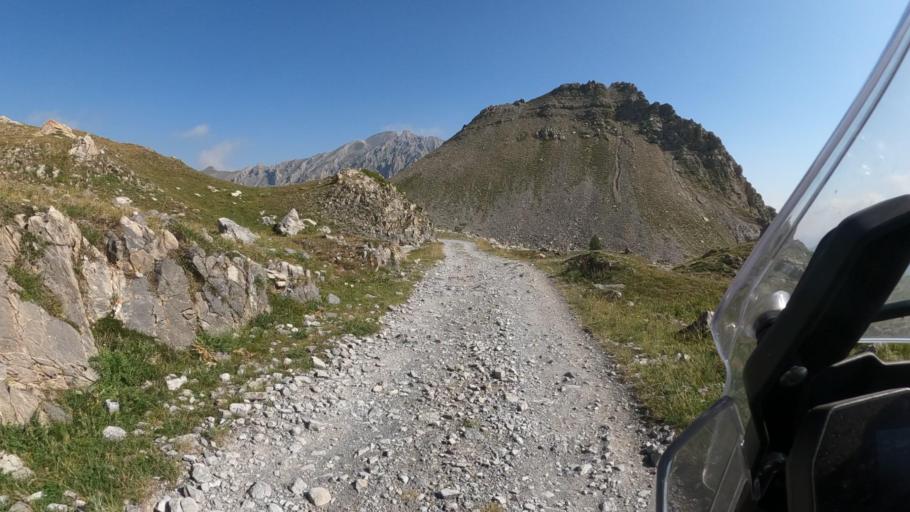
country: IT
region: Piedmont
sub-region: Provincia di Cuneo
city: Pietraporzio
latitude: 44.3953
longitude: 7.0235
